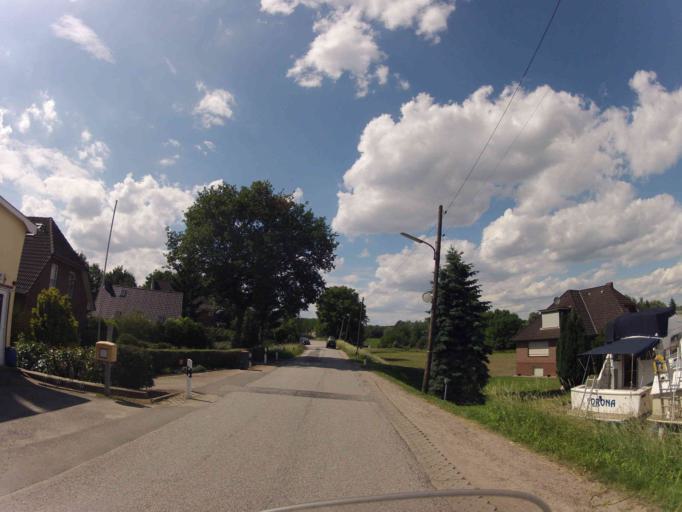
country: DE
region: Hamburg
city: Rothenburgsort
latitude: 53.4969
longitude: 10.0811
